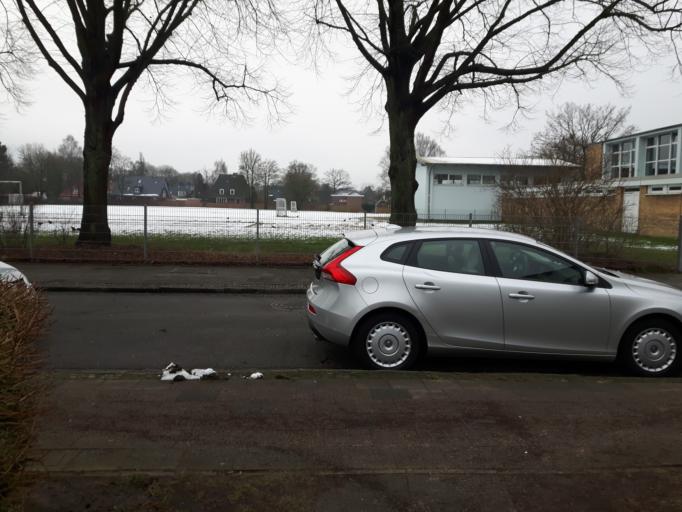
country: DE
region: Schleswig-Holstein
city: Neumunster
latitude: 54.0821
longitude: 9.9983
